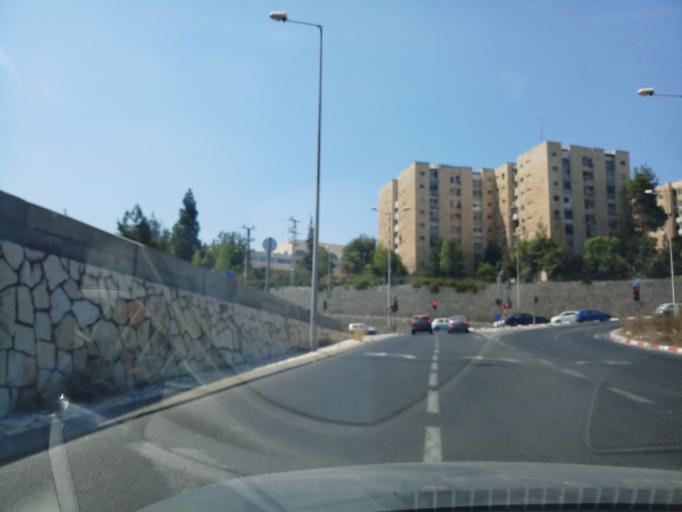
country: IL
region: Jerusalem
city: Jerusalem
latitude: 31.7673
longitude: 35.1959
